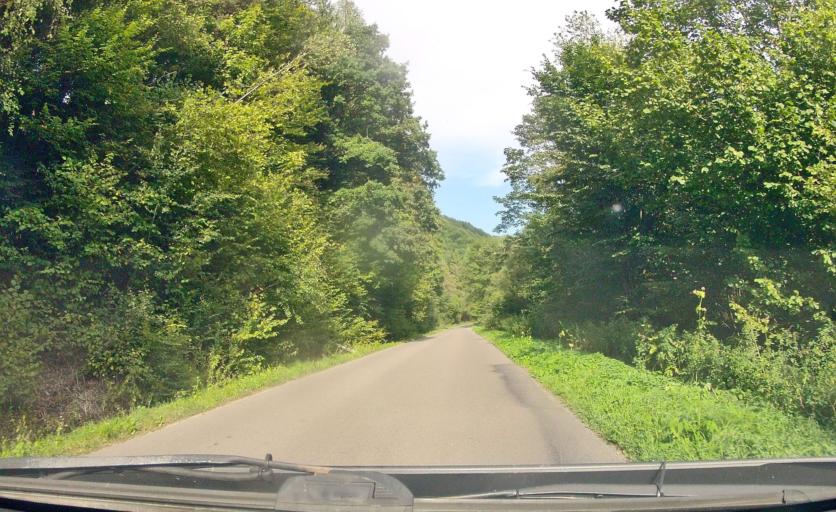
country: PL
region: Subcarpathian Voivodeship
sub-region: Powiat jasielski
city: Krempna
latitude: 49.4988
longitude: 21.5814
